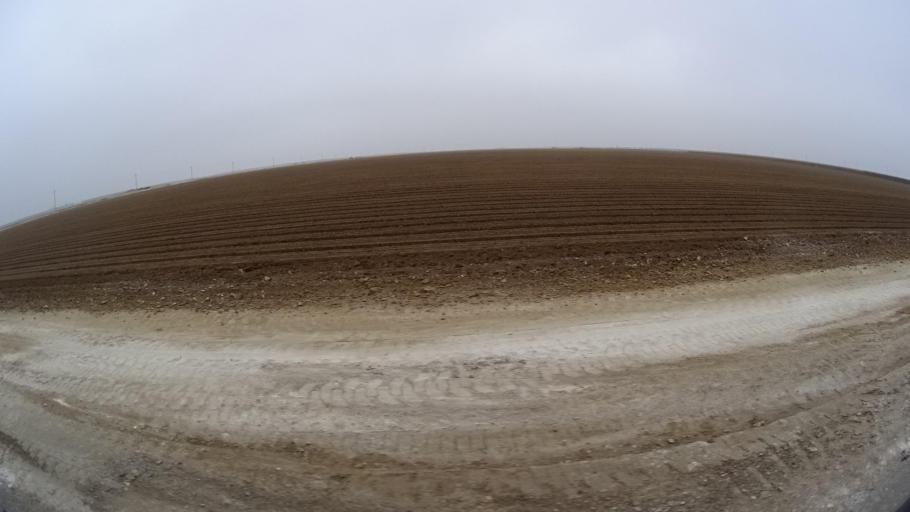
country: US
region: California
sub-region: Kern County
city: Lost Hills
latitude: 35.5955
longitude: -119.5269
